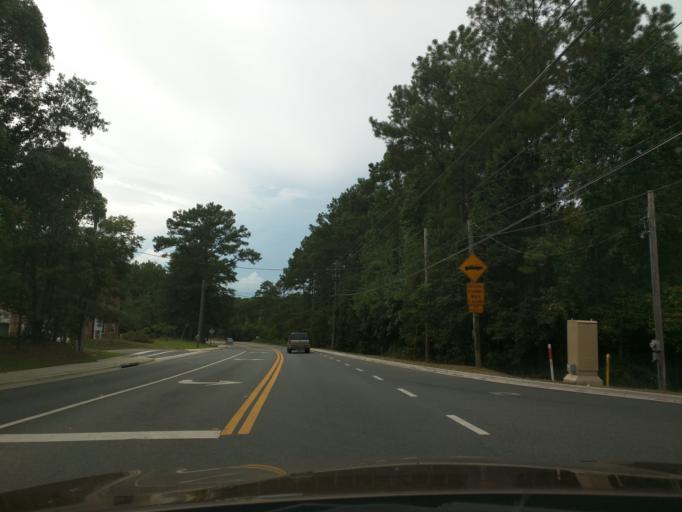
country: US
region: Florida
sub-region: Leon County
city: Tallahassee
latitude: 30.5870
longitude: -84.2523
